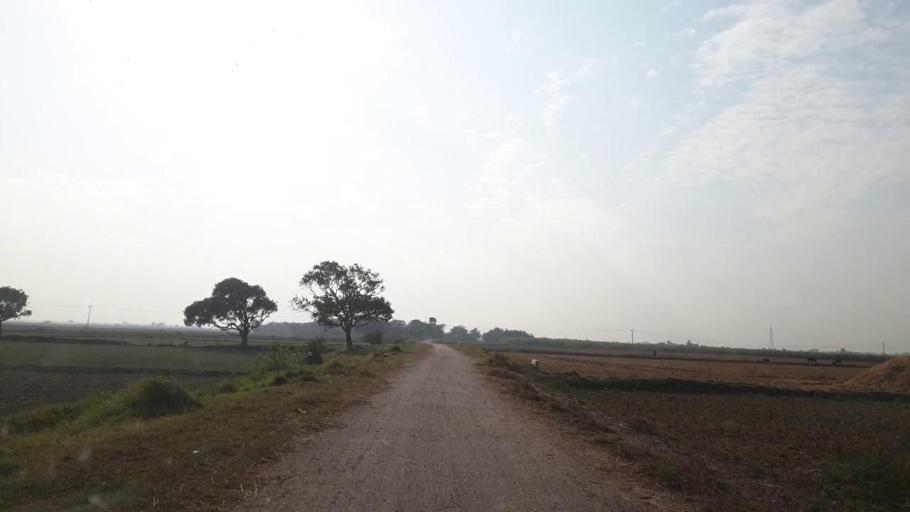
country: PK
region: Sindh
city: Chuhar Jamali
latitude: 24.3864
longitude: 68.0092
